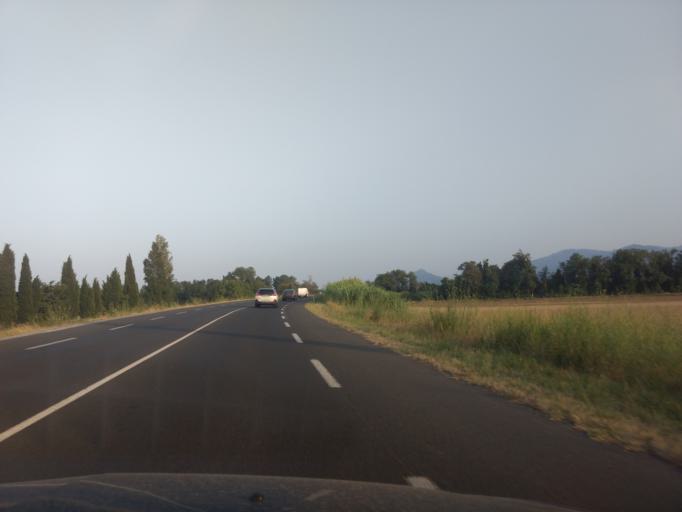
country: FR
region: Languedoc-Roussillon
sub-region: Departement des Pyrenees-Orientales
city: Latour-Bas-Elne
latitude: 42.5885
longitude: 3.0284
